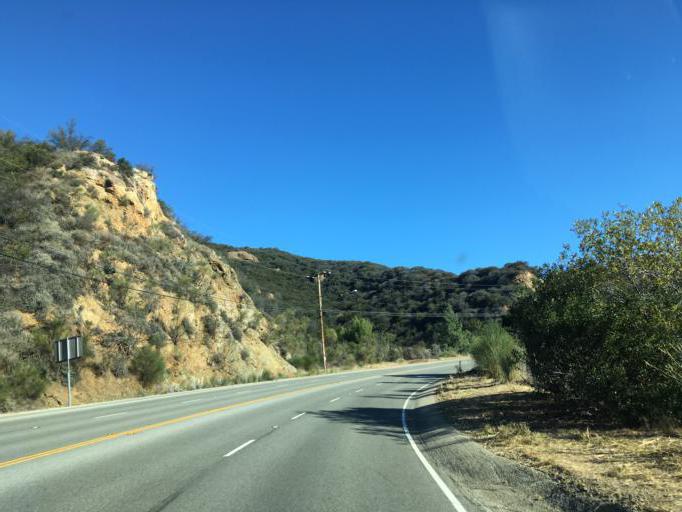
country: US
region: California
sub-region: Los Angeles County
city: Malibu
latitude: 34.0686
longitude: -118.8116
